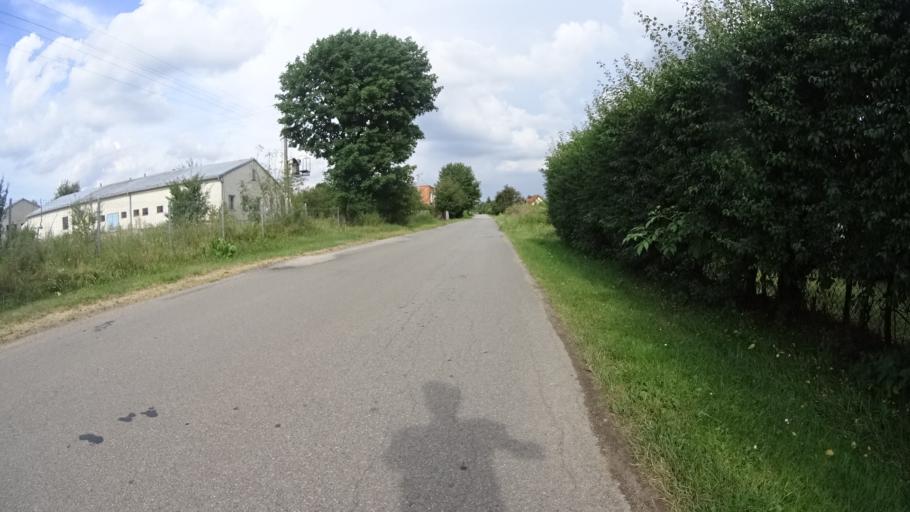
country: PL
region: Masovian Voivodeship
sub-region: Powiat grojecki
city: Goszczyn
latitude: 51.6966
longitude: 20.8306
